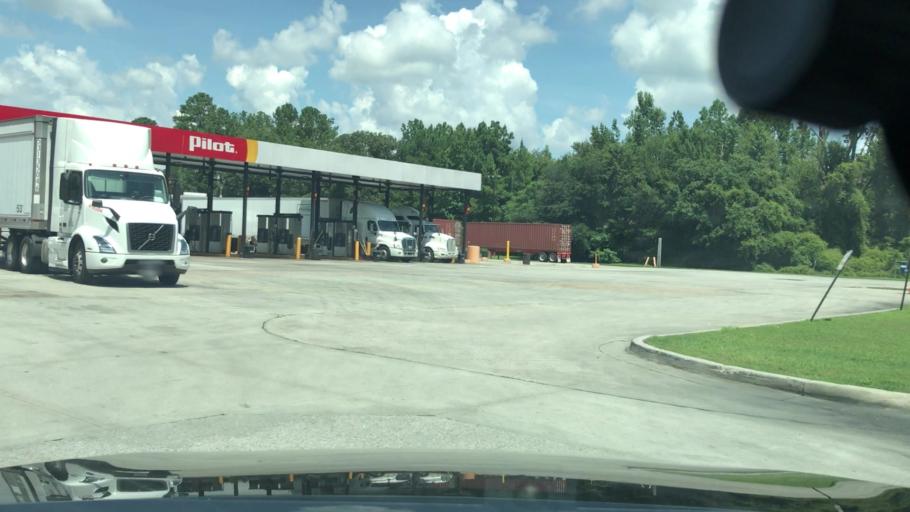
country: US
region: South Carolina
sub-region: Orangeburg County
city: Brookdale
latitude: 33.4171
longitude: -80.6659
